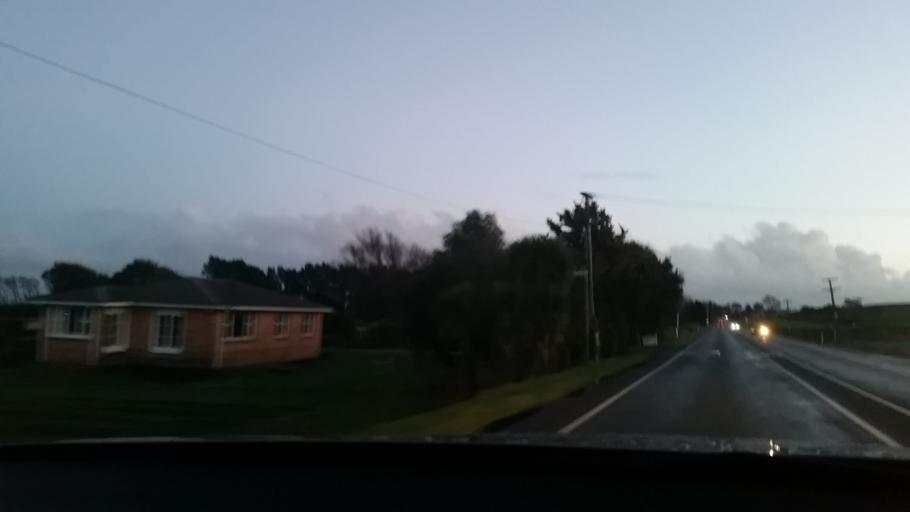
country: NZ
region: Waikato
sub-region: Hamilton City
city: Hamilton
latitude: -37.8098
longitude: 175.2368
